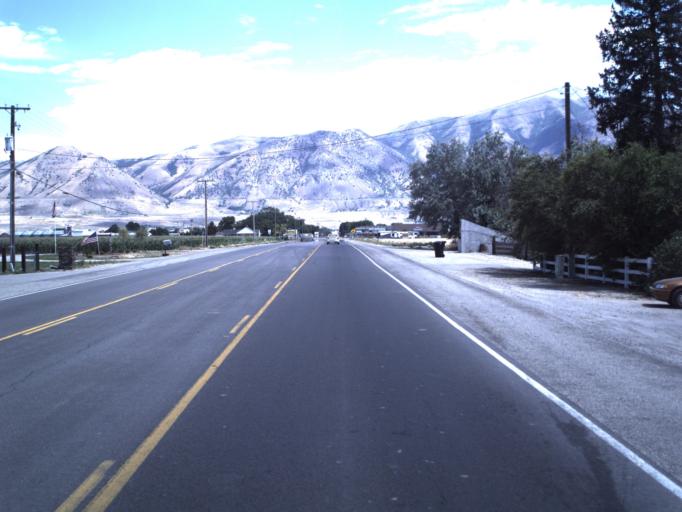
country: US
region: Utah
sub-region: Box Elder County
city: Tremonton
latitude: 41.7121
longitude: -112.1489
